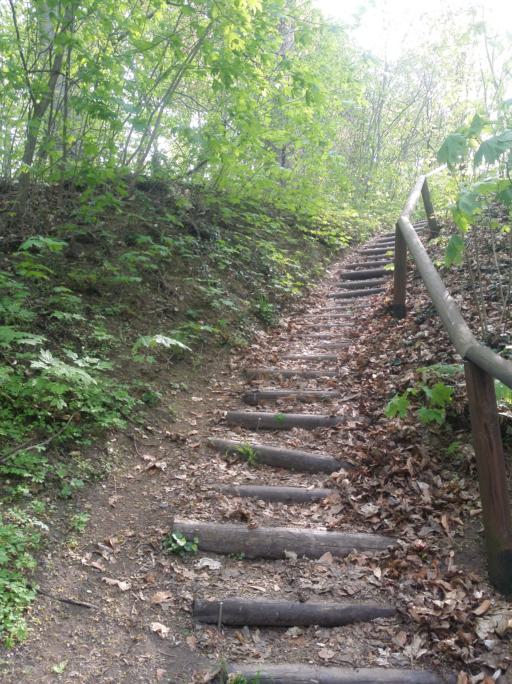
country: DE
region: Saxony-Anhalt
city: Neinstedt
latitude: 51.7313
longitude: 11.0891
